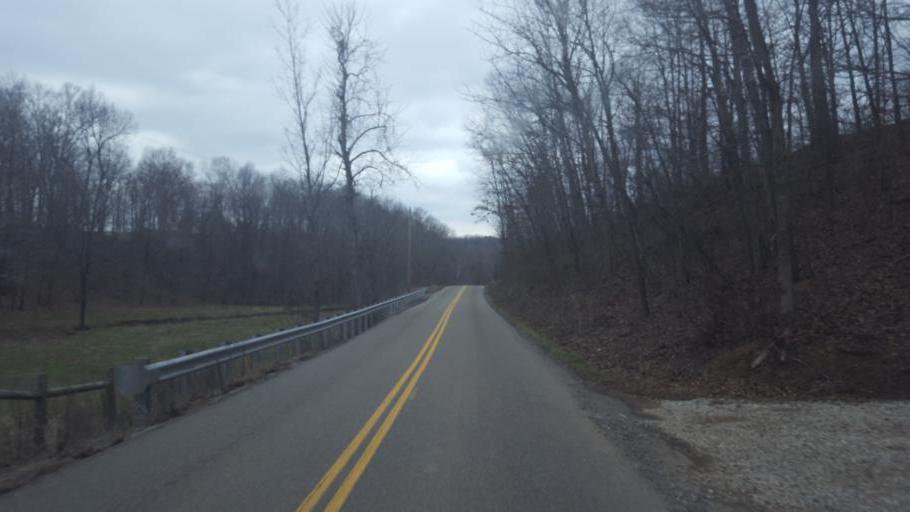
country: US
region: Ohio
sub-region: Gallia County
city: Gallipolis
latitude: 38.7185
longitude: -82.3481
